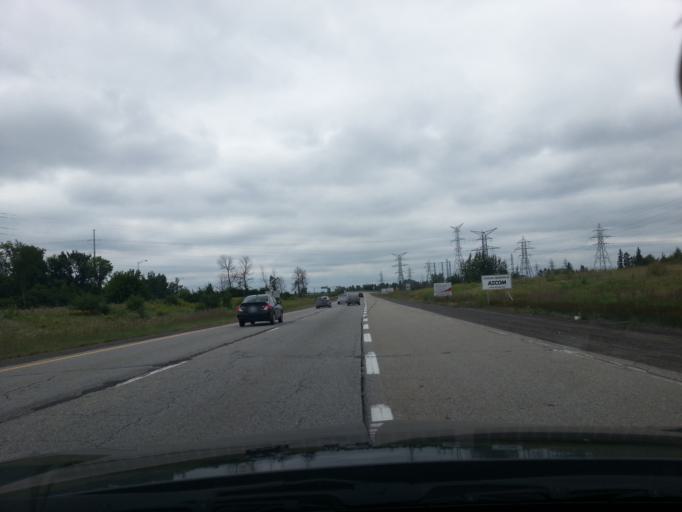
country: CA
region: Ontario
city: Ottawa
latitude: 45.3970
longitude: -75.5931
